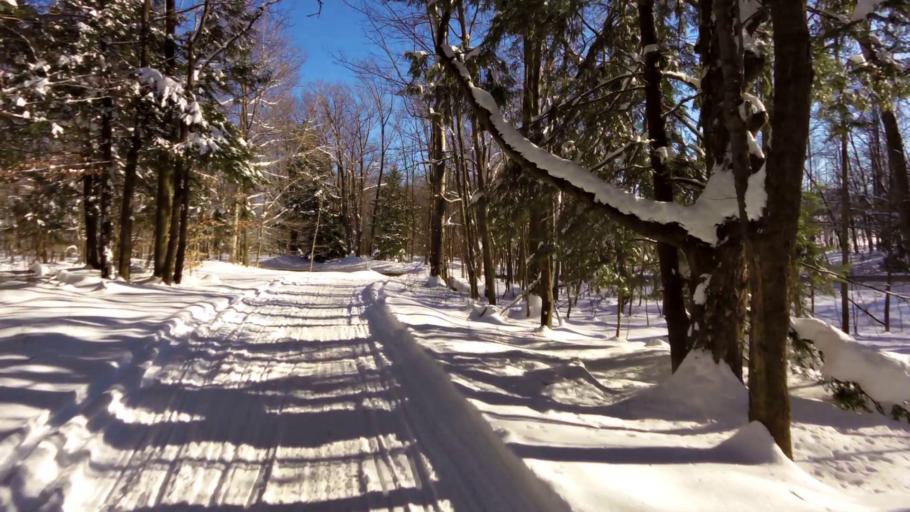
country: US
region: New York
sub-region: Chautauqua County
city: Mayville
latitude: 42.1499
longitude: -79.5745
